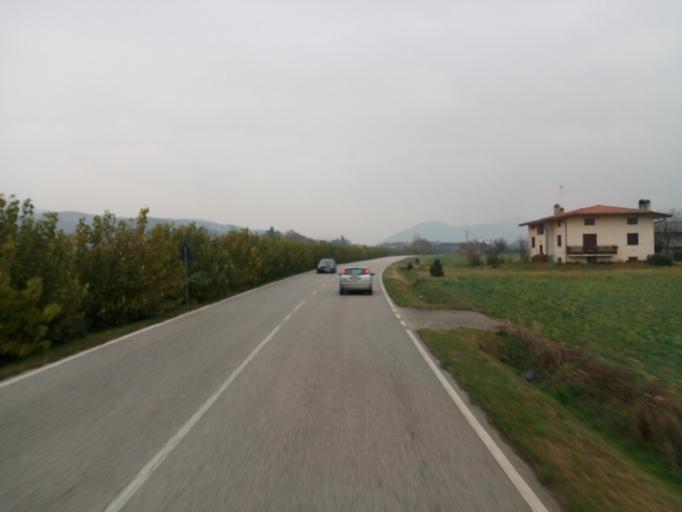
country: IT
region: Friuli Venezia Giulia
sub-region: Provincia di Udine
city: Cividale del Friuli
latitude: 46.0951
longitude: 13.4109
